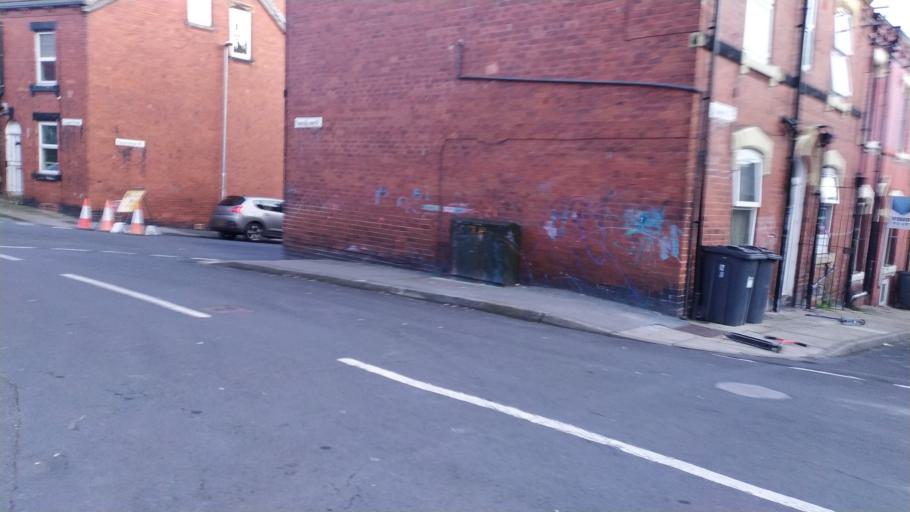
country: GB
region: England
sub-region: City and Borough of Leeds
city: Leeds
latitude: 53.8151
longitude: -1.5537
